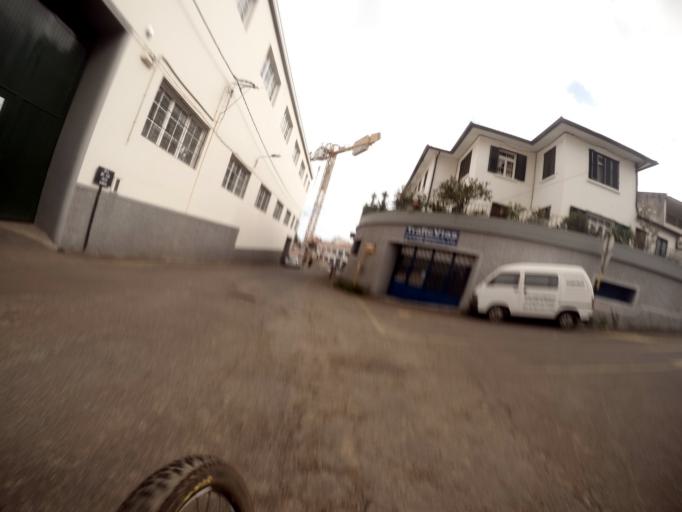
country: PT
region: Madeira
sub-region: Funchal
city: Nossa Senhora do Monte
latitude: 32.6509
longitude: -16.9195
